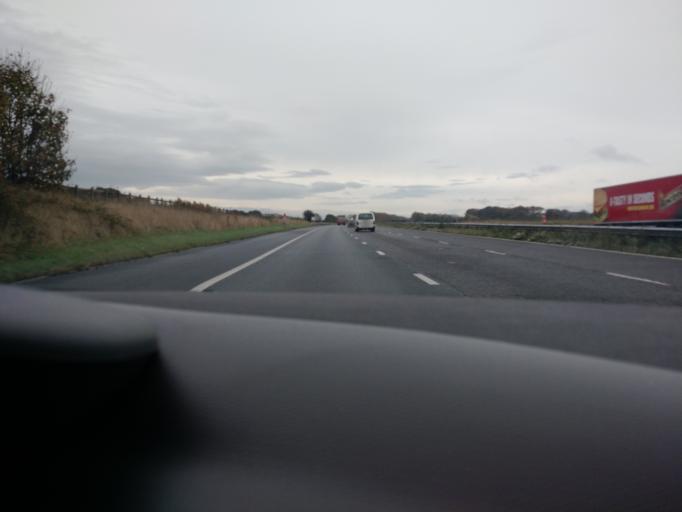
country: GB
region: England
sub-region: Lancashire
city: Kirkham
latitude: 53.8070
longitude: -2.8561
